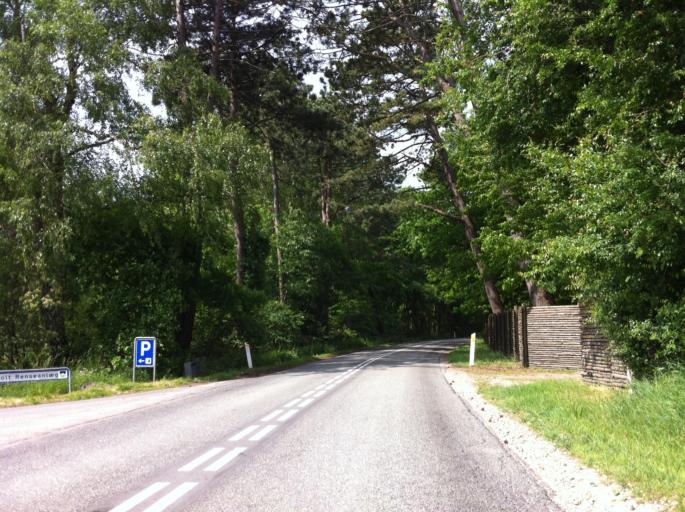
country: DK
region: Capital Region
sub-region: Gribskov Kommune
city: Helsinge
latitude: 56.1063
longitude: 12.1844
